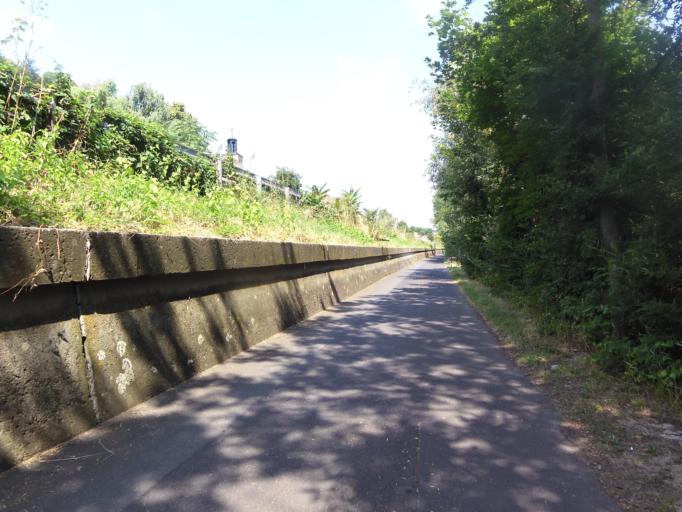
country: DE
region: Bavaria
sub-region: Regierungsbezirk Unterfranken
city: Zell am Main
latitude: 49.8059
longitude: 9.8758
